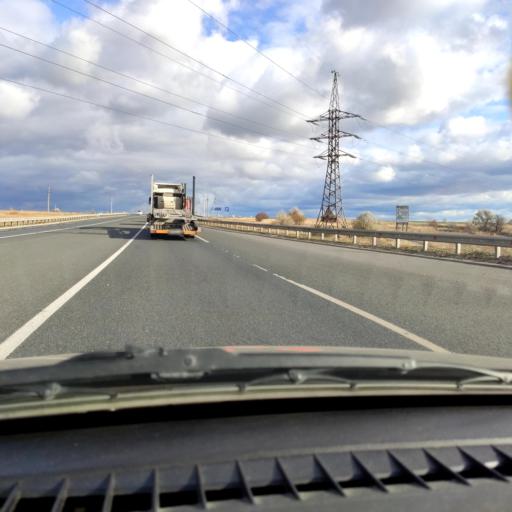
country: RU
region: Samara
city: Varlamovo
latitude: 53.2037
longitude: 48.3819
